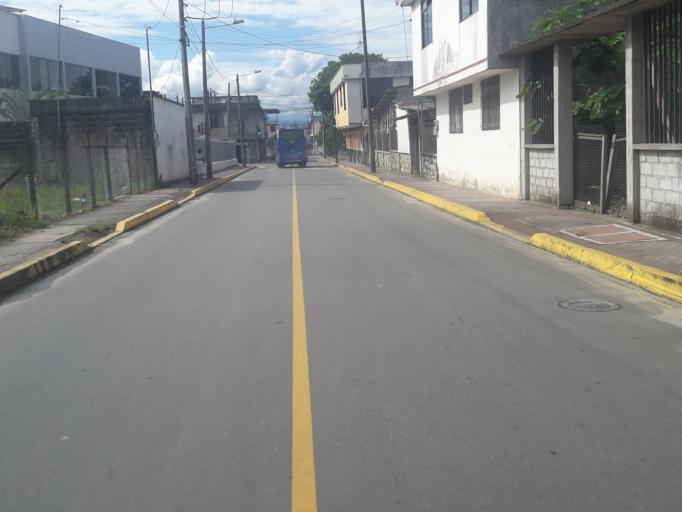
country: EC
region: Napo
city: Tena
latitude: -1.0078
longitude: -77.8128
